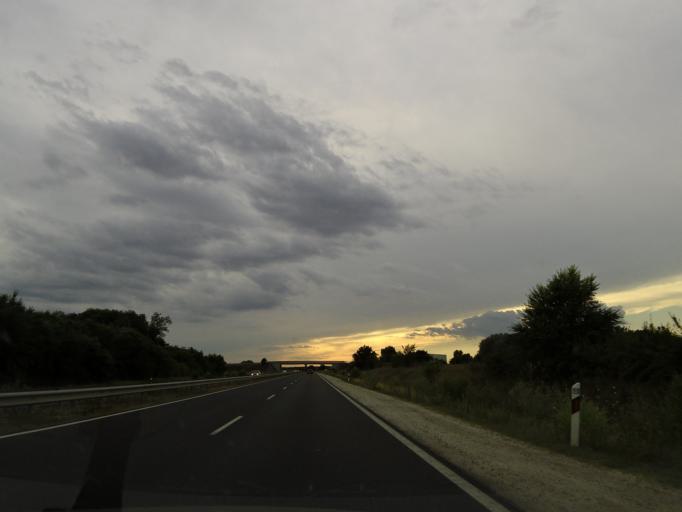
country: HU
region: Pest
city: Vecses
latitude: 47.4142
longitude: 19.2869
